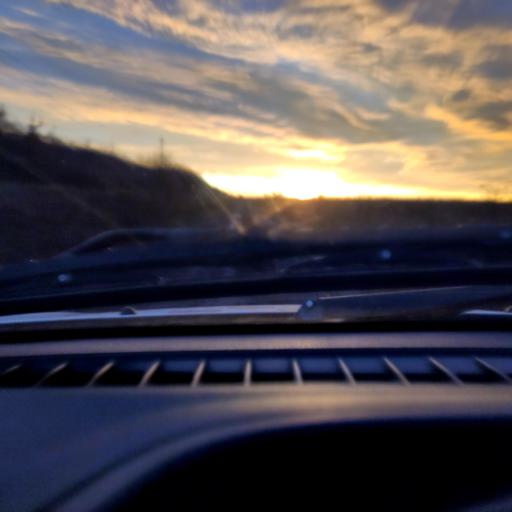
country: RU
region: Samara
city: Tol'yatti
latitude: 53.5975
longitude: 49.4630
